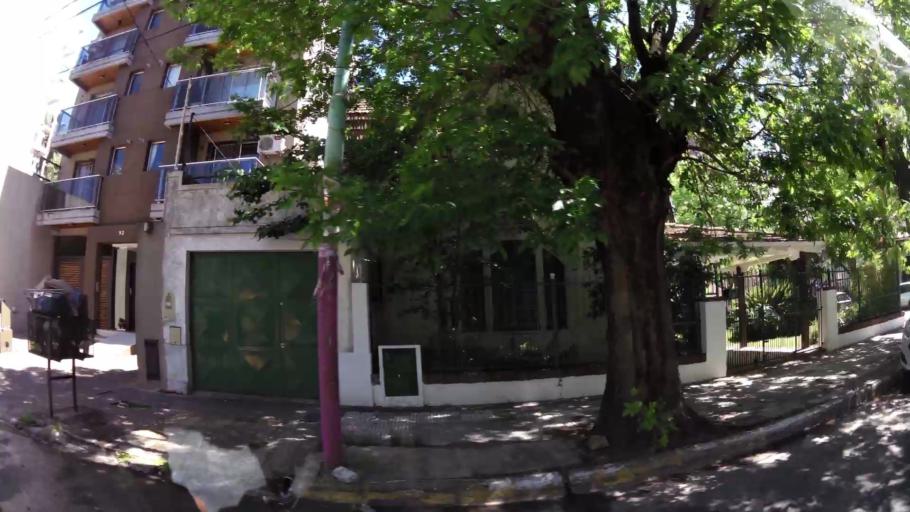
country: AR
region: Buenos Aires
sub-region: Partido de Quilmes
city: Quilmes
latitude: -34.7192
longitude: -58.2623
